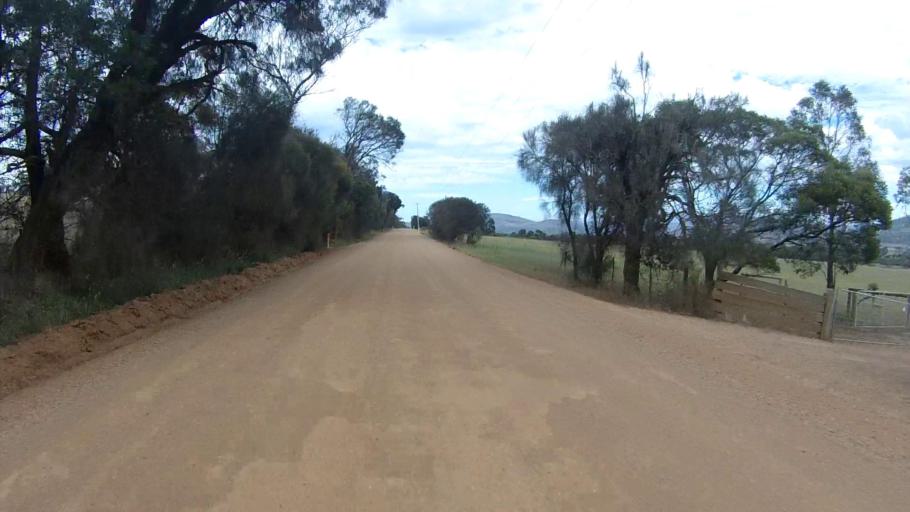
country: AU
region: Tasmania
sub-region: Clarence
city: Cambridge
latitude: -42.7029
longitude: 147.4577
